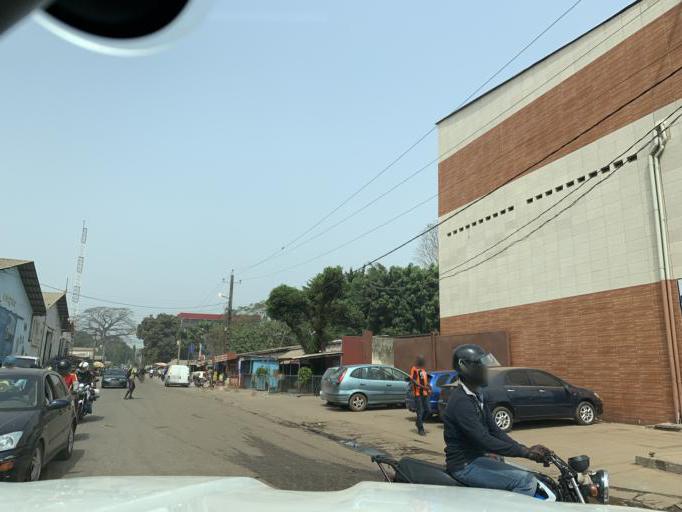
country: GN
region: Conakry
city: Conakry
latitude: 9.5321
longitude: -13.6806
